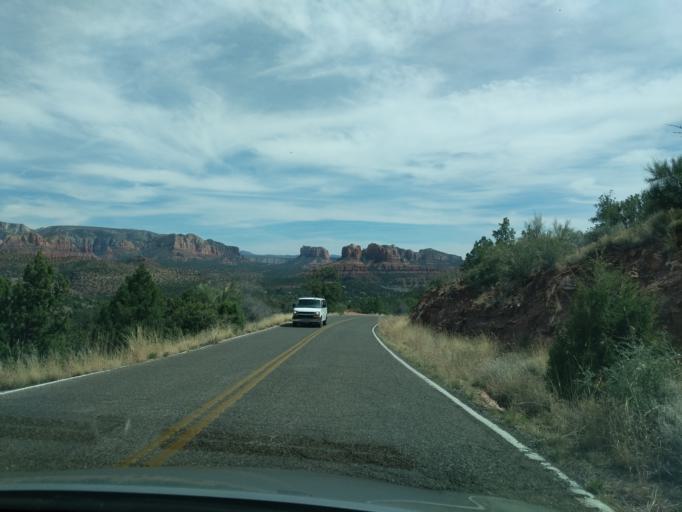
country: US
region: Arizona
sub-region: Yavapai County
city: West Sedona
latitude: 34.8424
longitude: -111.8273
